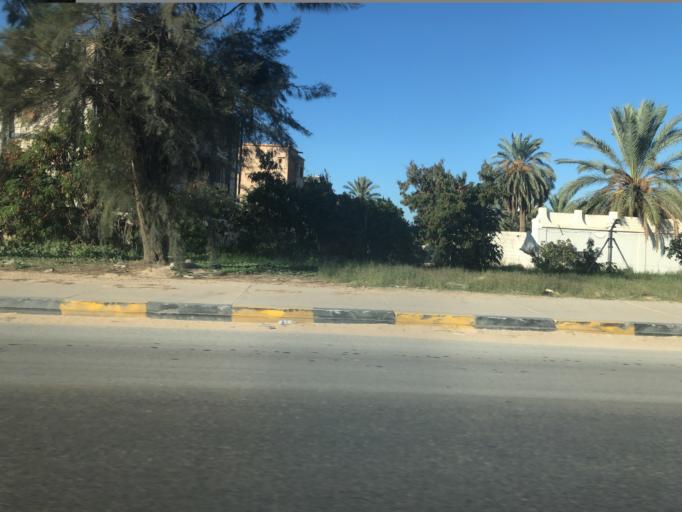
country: LY
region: Tripoli
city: Tripoli
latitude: 32.8693
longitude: 13.2589
